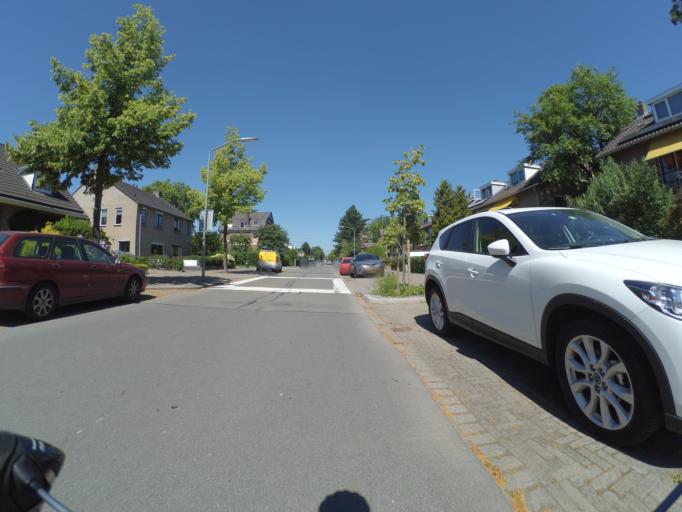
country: NL
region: South Holland
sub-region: Gemeente Dordrecht
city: Dordrecht
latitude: 51.8004
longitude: 4.6847
